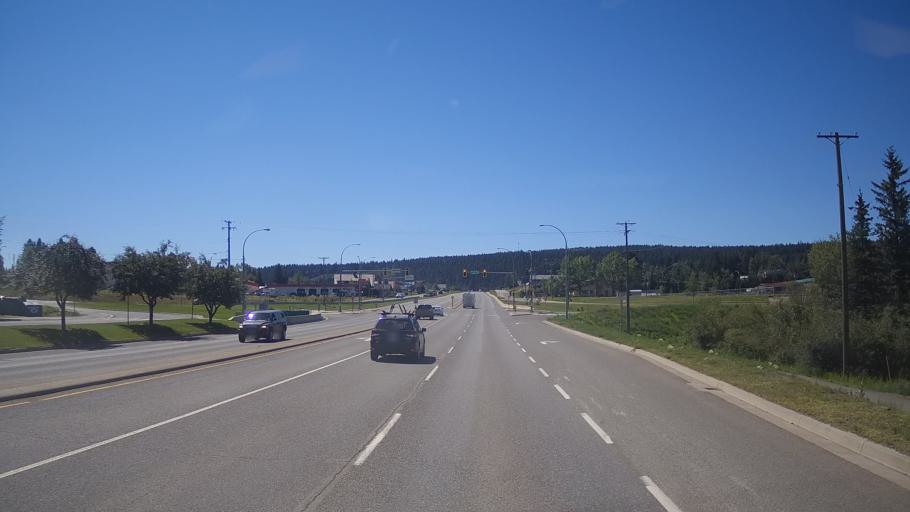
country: CA
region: British Columbia
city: Cache Creek
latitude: 51.6393
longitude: -121.2983
